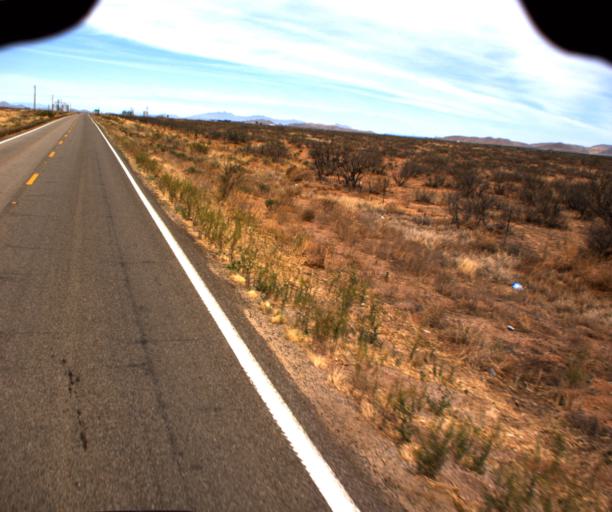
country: US
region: Arizona
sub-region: Cochise County
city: Bisbee
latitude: 31.7400
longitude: -109.6879
